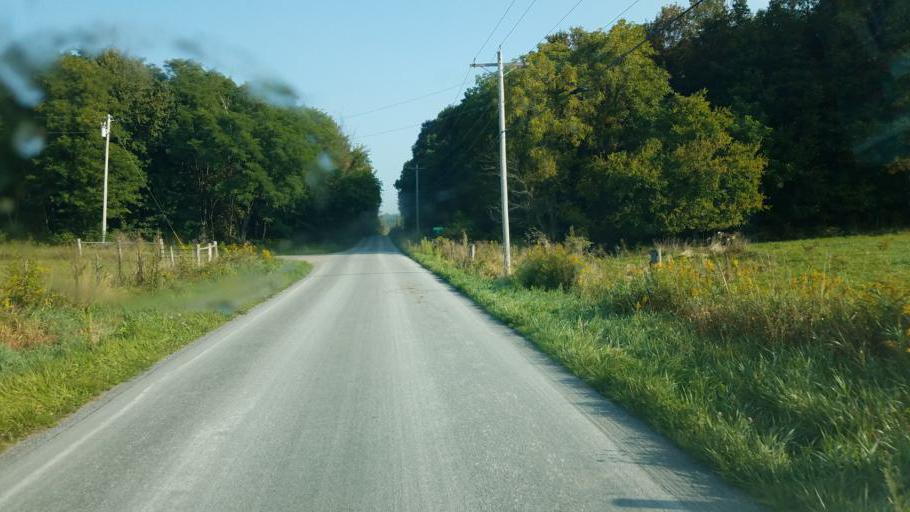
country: US
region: Ohio
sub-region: Knox County
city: Fredericktown
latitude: 40.5347
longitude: -82.6332
